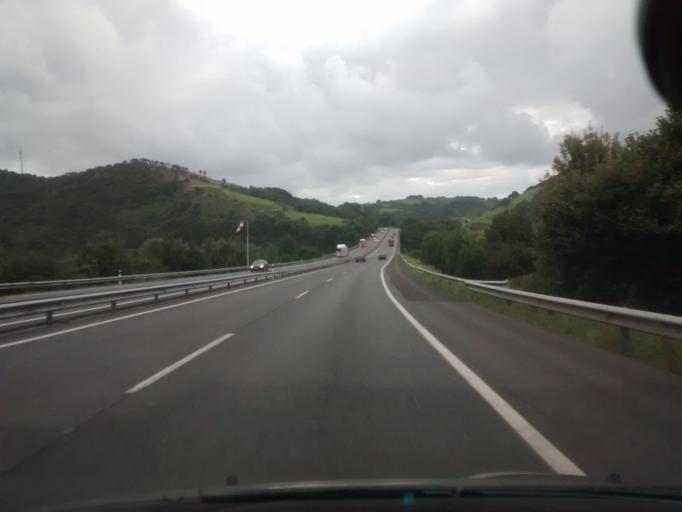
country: ES
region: Basque Country
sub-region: Provincia de Guipuzcoa
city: Orio
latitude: 43.2823
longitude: -2.1240
